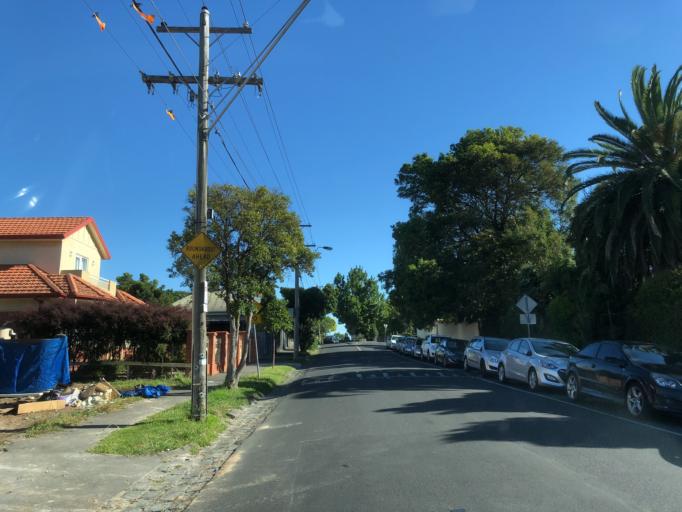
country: AU
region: Victoria
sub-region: Moonee Valley
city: Moonee Ponds
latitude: -37.7646
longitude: 144.9276
